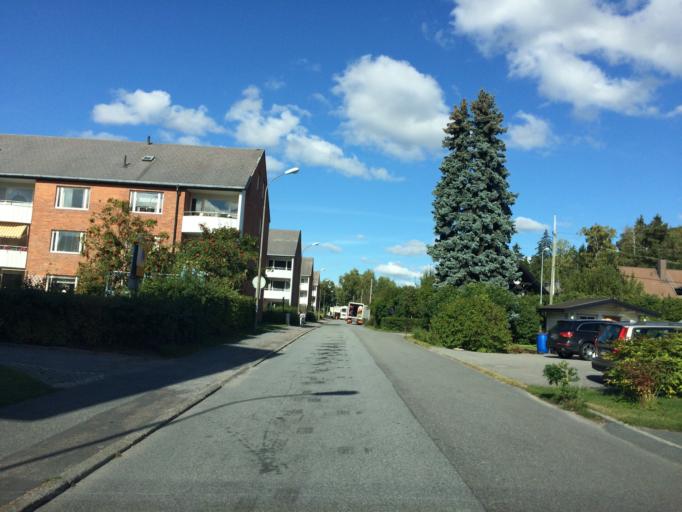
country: SE
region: Stockholm
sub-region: Sollentuna Kommun
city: Sollentuna
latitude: 59.4443
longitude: 17.9286
